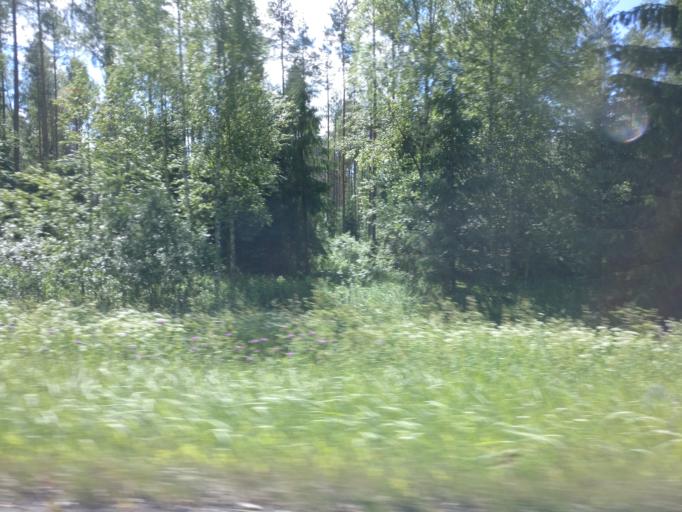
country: FI
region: Southern Savonia
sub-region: Savonlinna
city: Savonlinna
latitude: 61.8771
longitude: 28.9955
